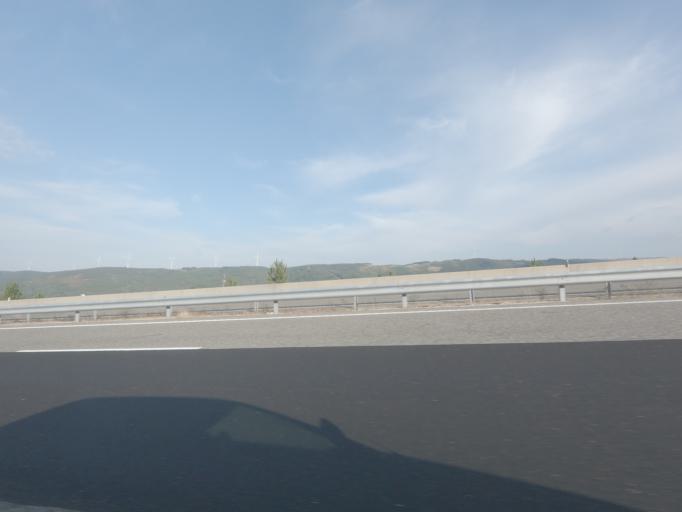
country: PT
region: Vila Real
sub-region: Vila Pouca de Aguiar
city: Vila Pouca de Aguiar
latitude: 41.5300
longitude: -7.6373
